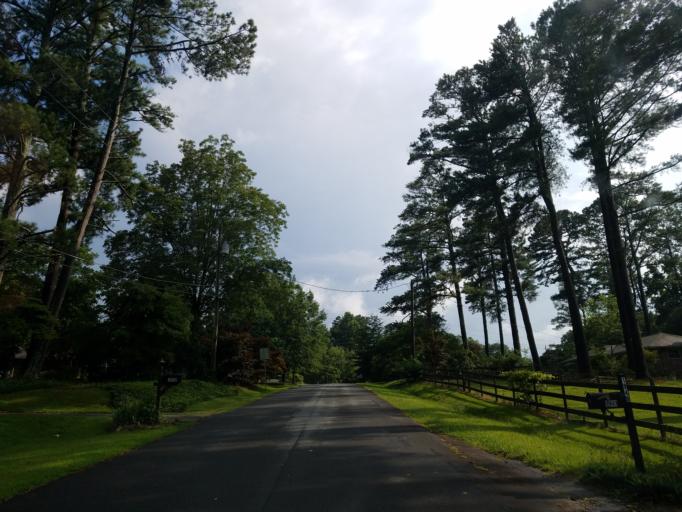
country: US
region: Georgia
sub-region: Cobb County
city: Marietta
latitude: 33.9987
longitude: -84.5432
